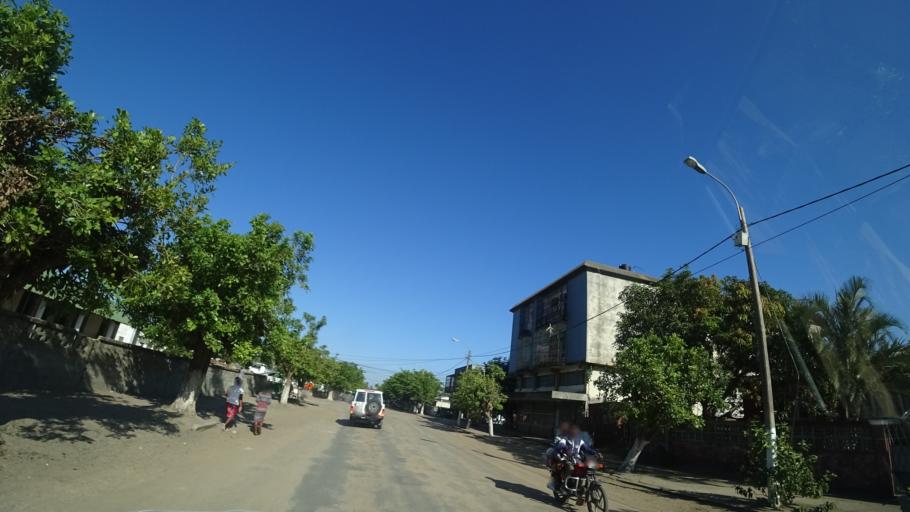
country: MZ
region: Sofala
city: Dondo
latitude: -19.6157
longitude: 34.7448
